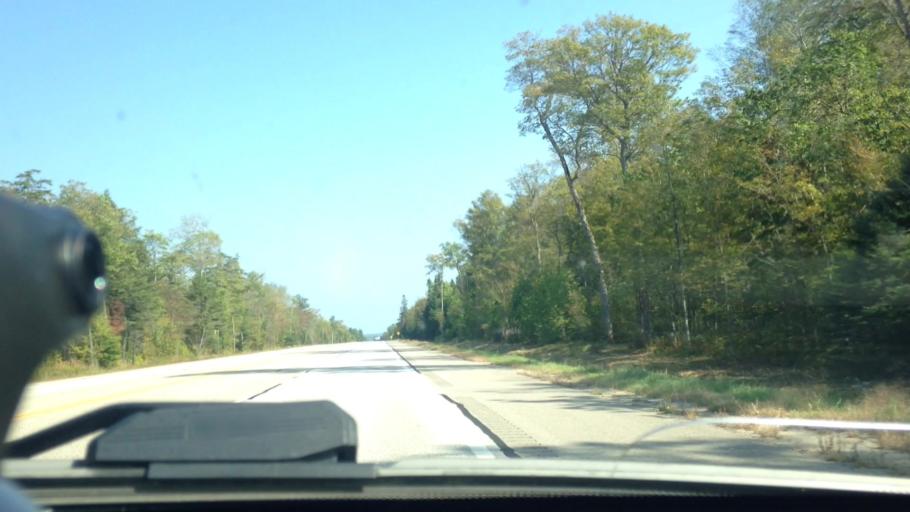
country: US
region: Michigan
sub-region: Luce County
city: Newberry
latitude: 46.3035
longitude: -85.2702
